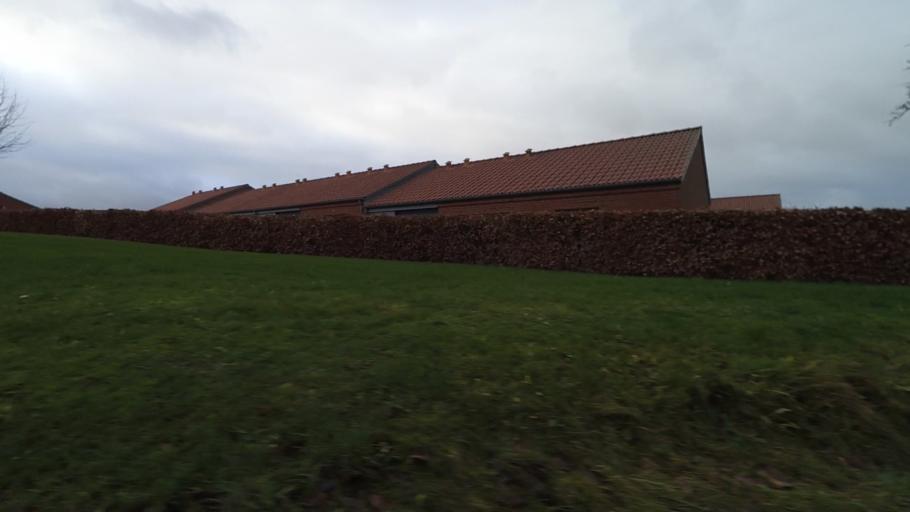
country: DK
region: Central Jutland
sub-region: Arhus Kommune
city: Marslet
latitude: 56.1024
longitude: 10.1725
